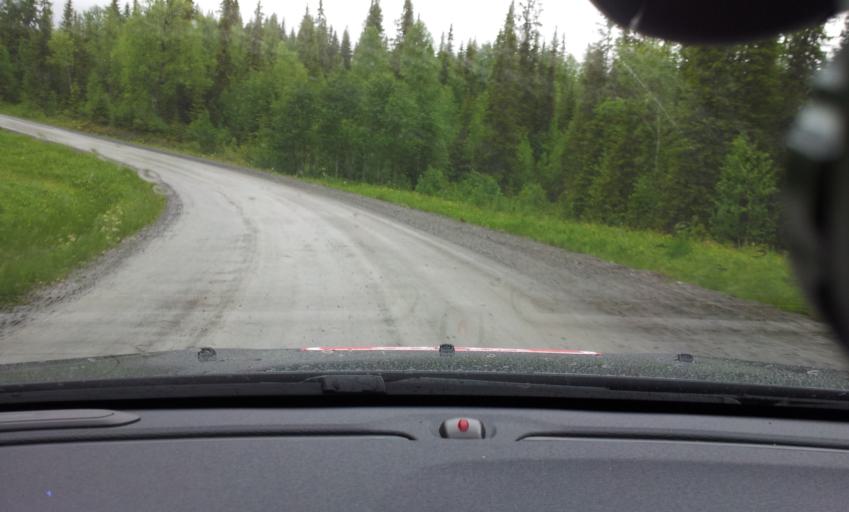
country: SE
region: Jaemtland
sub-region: Are Kommun
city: Are
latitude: 63.4329
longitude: 12.8052
